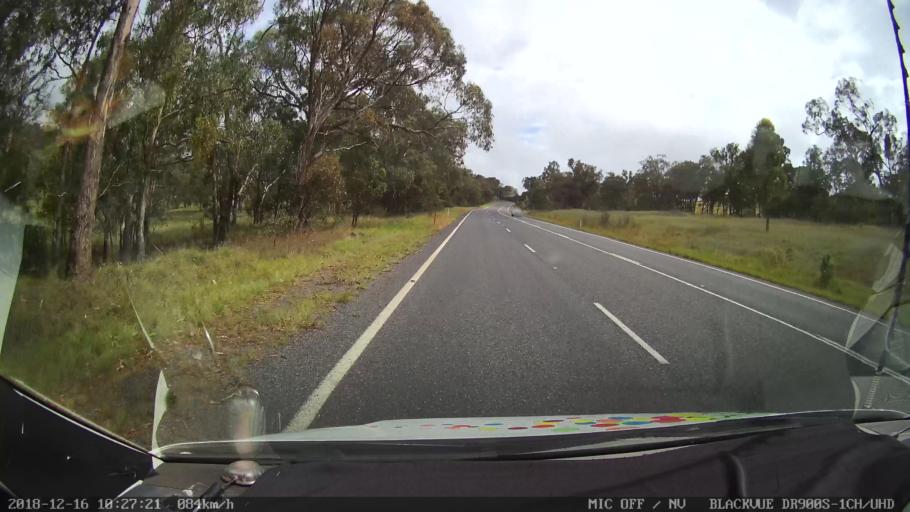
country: AU
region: New South Wales
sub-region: Tenterfield Municipality
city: Carrolls Creek
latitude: -29.1347
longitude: 151.9954
